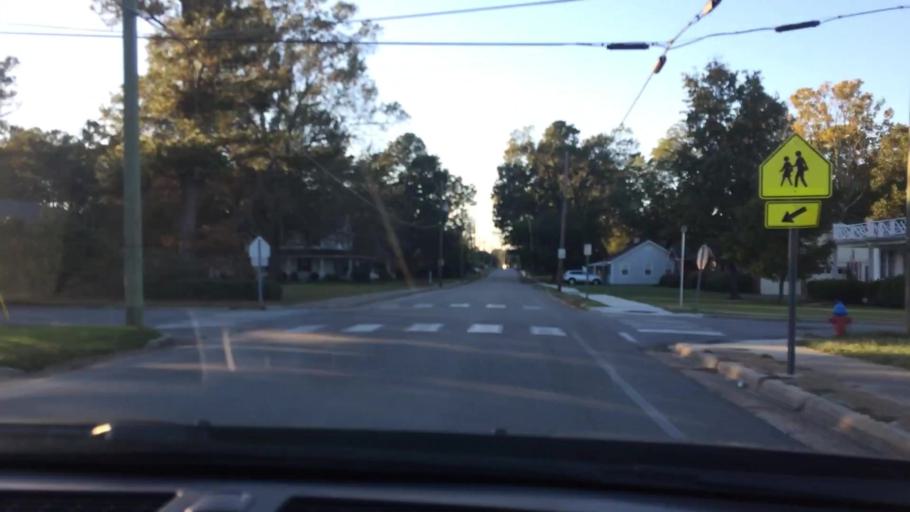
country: US
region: North Carolina
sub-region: Pitt County
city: Farmville
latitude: 35.5948
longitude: -77.5776
